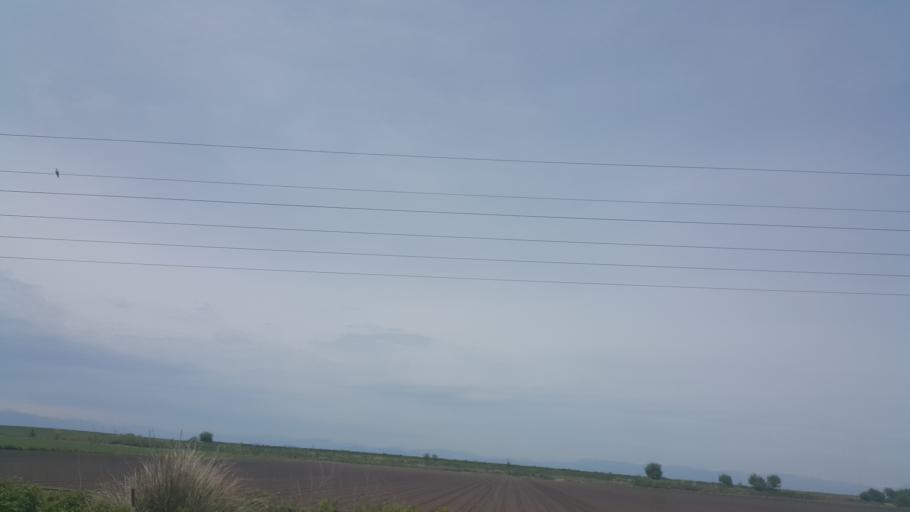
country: TR
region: Adana
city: Kosreli
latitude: 37.0672
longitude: 35.9841
